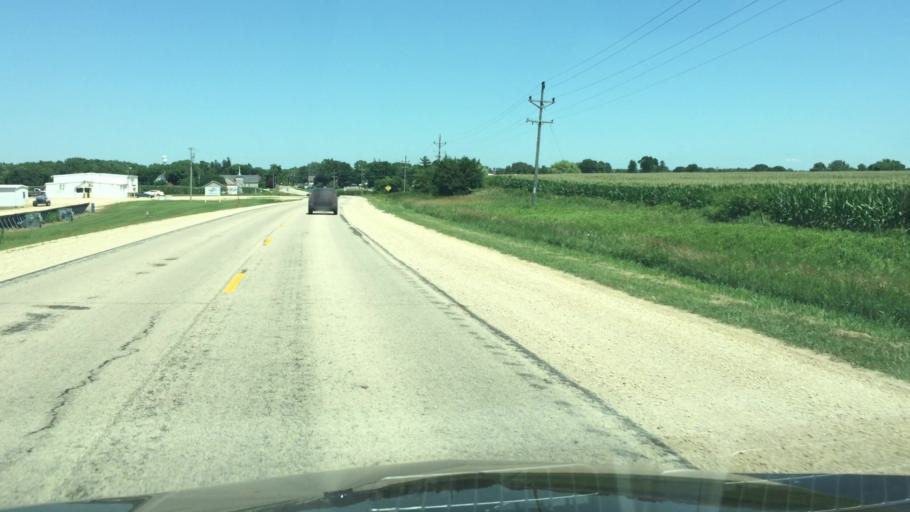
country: US
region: Iowa
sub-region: Cedar County
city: Mechanicsville
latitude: 41.9872
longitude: -91.1418
